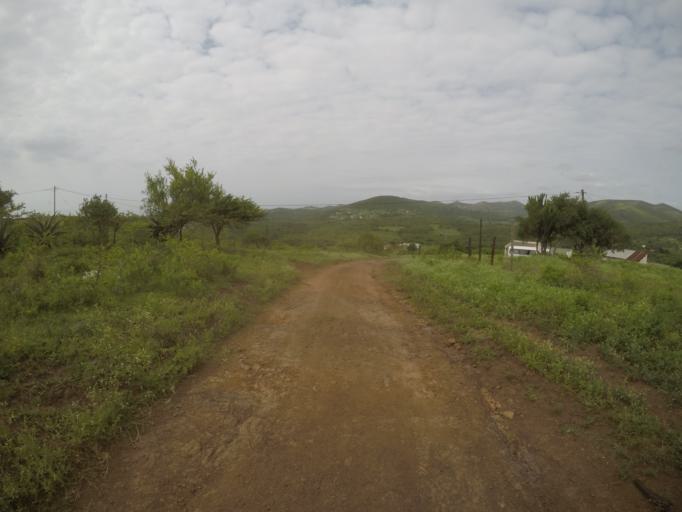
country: ZA
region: KwaZulu-Natal
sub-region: uThungulu District Municipality
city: Empangeni
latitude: -28.6263
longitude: 31.9015
